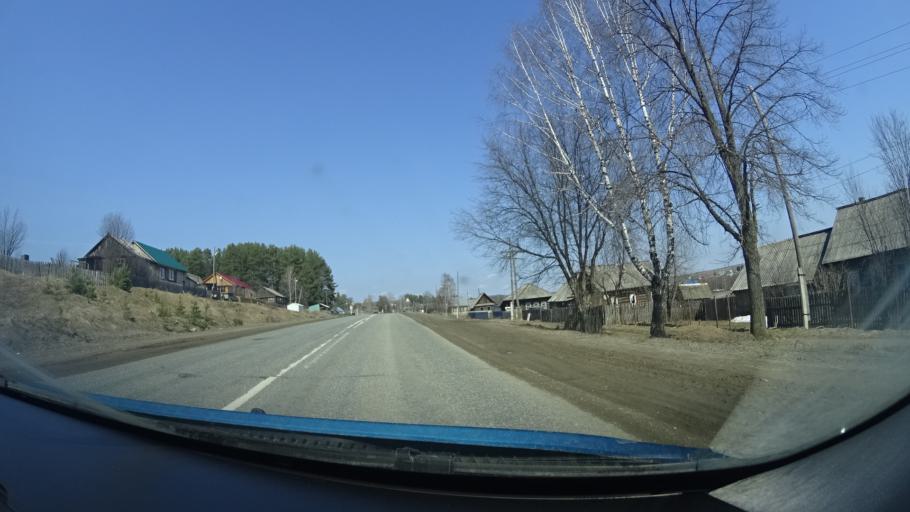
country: RU
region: Perm
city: Yugo-Kamskiy
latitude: 57.5503
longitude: 55.6853
